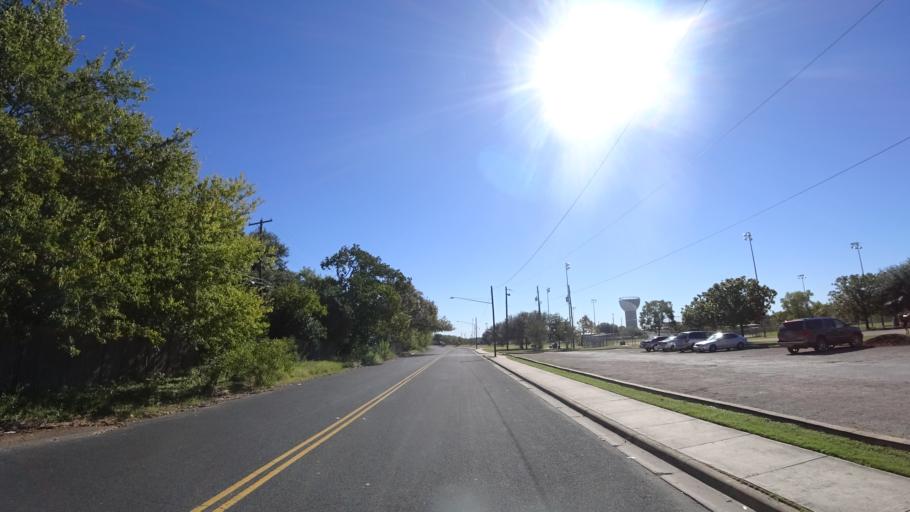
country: US
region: Texas
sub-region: Travis County
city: Austin
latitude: 30.3054
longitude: -97.6970
